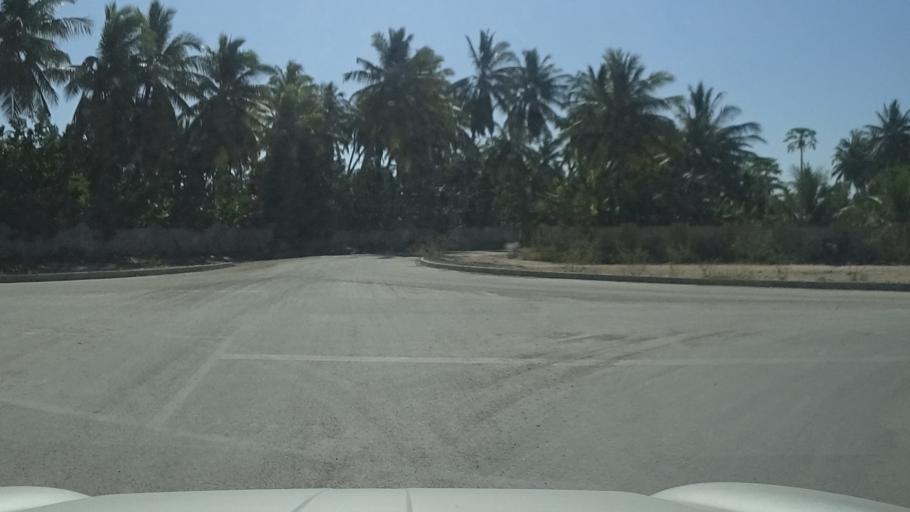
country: OM
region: Zufar
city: Salalah
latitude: 17.0322
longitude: 54.1451
